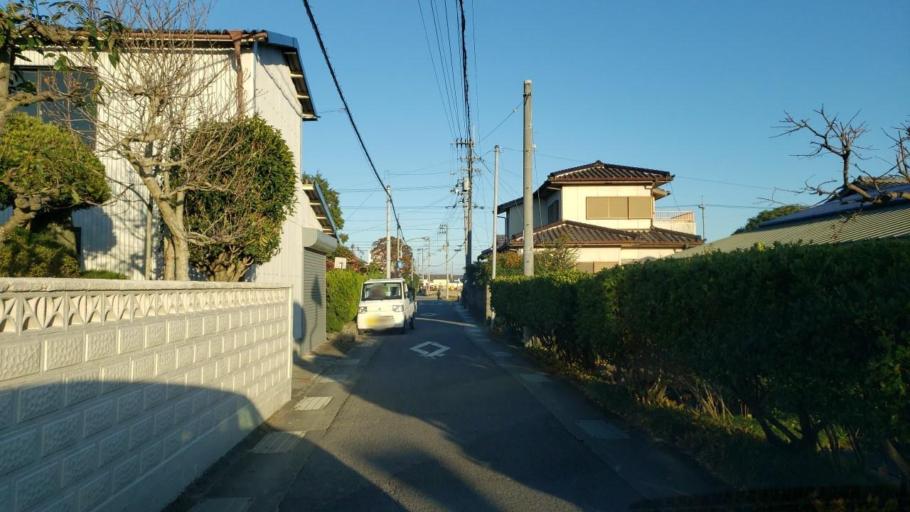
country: JP
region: Tokushima
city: Kamojimacho-jogejima
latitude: 34.0948
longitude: 134.2881
